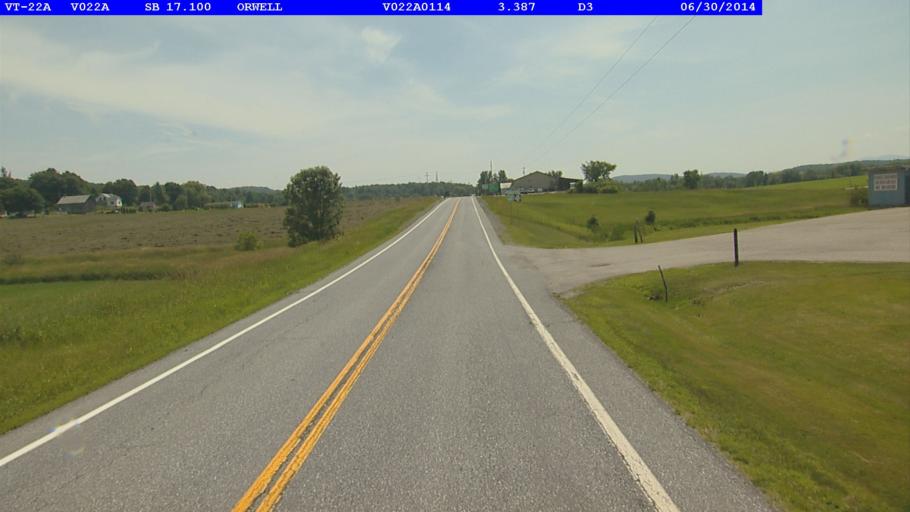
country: US
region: New York
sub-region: Essex County
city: Ticonderoga
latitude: 43.8058
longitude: -73.3048
